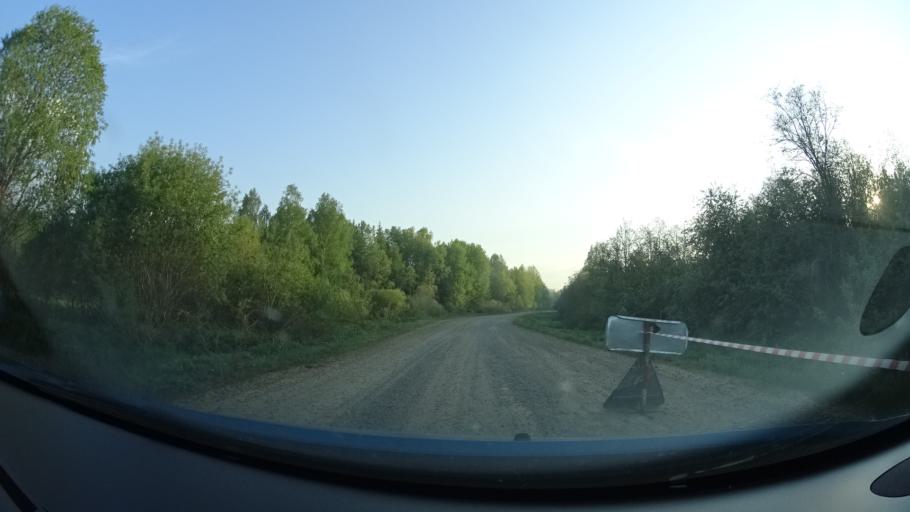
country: RU
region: Perm
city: Kuyeda
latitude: 56.6261
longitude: 55.7094
